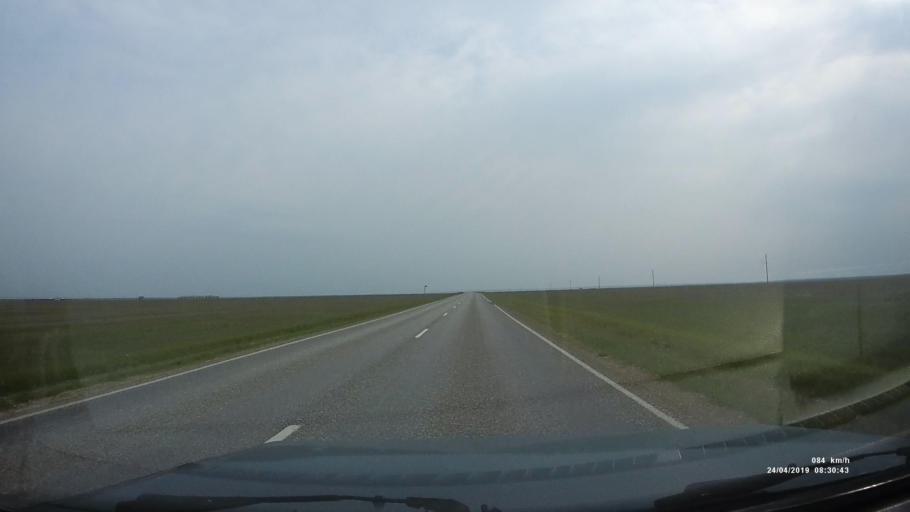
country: RU
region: Kalmykiya
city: Priyutnoye
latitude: 46.1614
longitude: 43.8494
